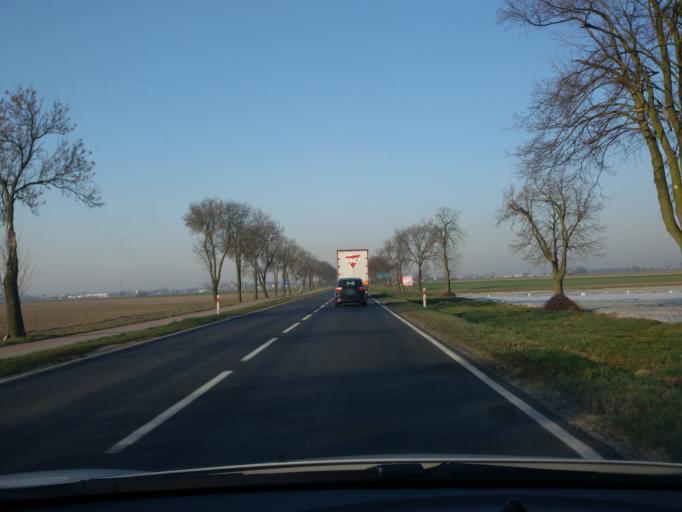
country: PL
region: Lubusz
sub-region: Powiat wschowski
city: Wschowa
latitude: 51.8189
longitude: 16.3494
